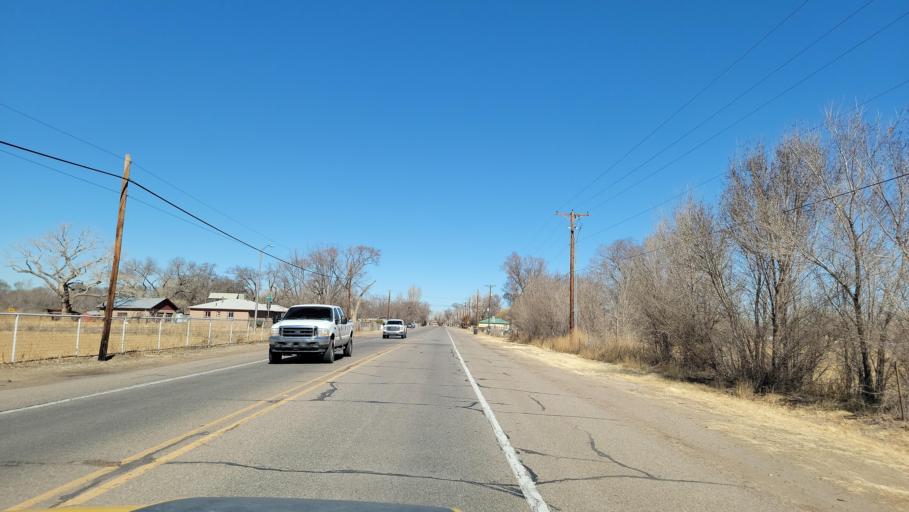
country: US
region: New Mexico
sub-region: Bernalillo County
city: South Valley
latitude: 34.9676
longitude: -106.6956
